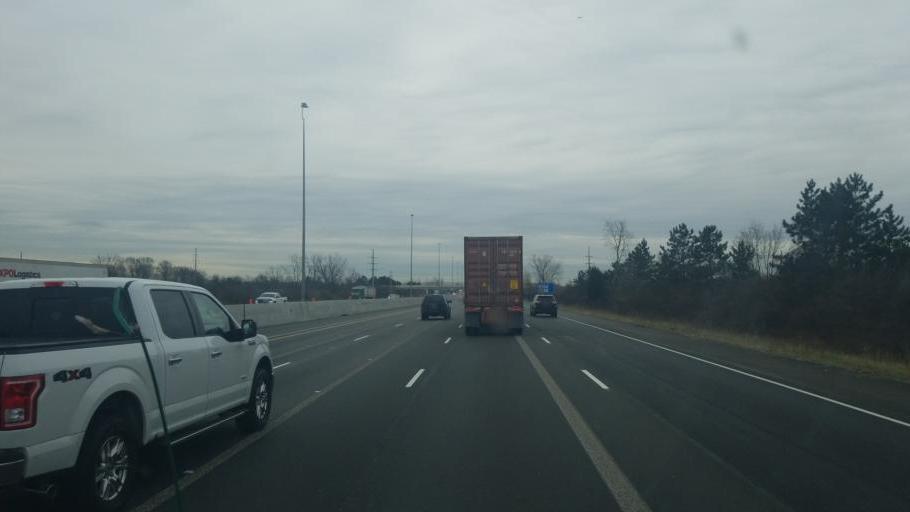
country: US
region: Ohio
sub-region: Franklin County
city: Hilliard
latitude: 40.0545
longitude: -83.1299
